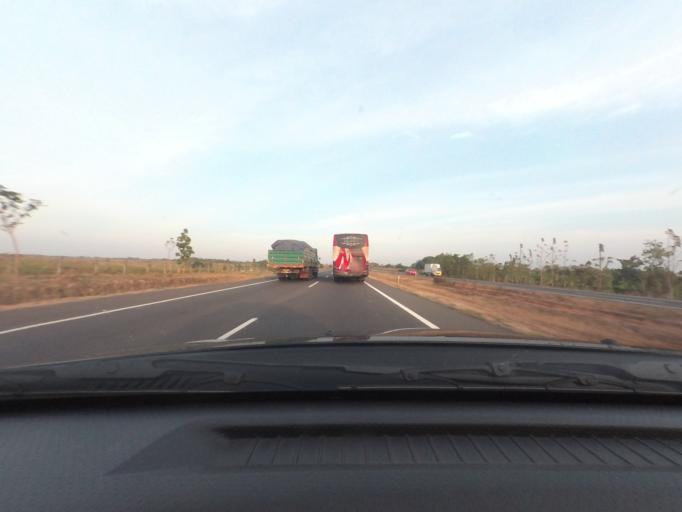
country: ID
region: West Java
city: Pamanukan
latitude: -6.5316
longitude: 107.8220
